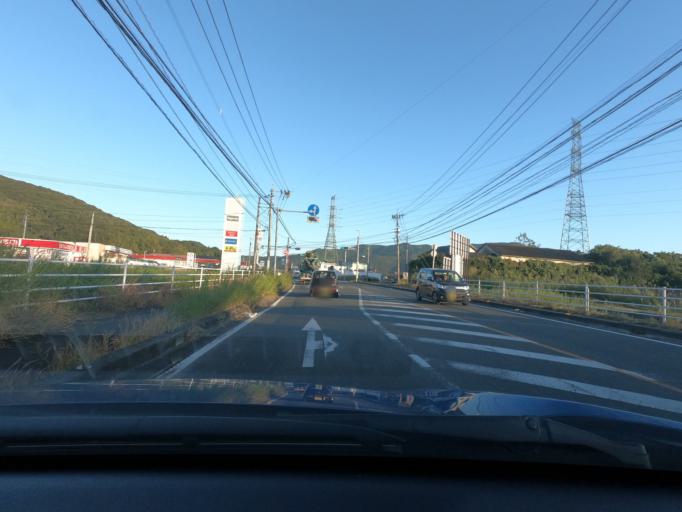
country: JP
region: Kagoshima
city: Satsumasendai
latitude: 31.8082
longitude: 130.3373
